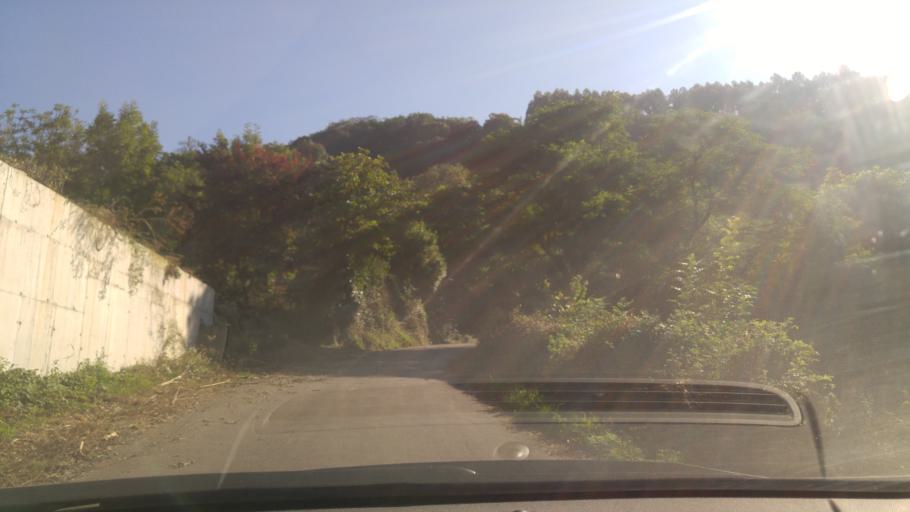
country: ES
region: Asturias
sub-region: Province of Asturias
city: Barzana
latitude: 43.1692
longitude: -5.9862
